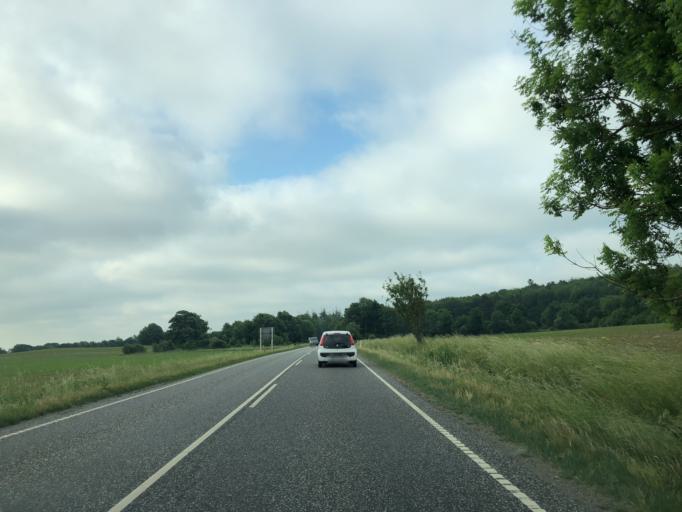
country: DK
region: South Denmark
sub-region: Vejle Kommune
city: Give
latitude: 55.7681
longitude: 9.2903
